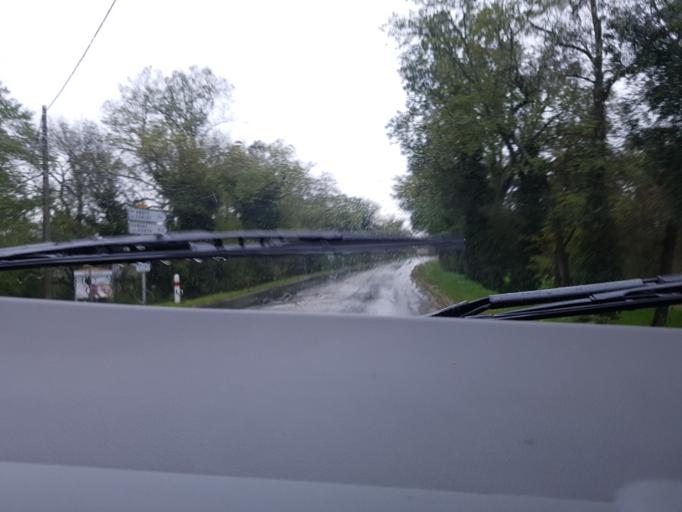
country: FR
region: Aquitaine
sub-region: Departement de la Gironde
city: Cubzac-les-Ponts
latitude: 44.9671
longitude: -0.4547
